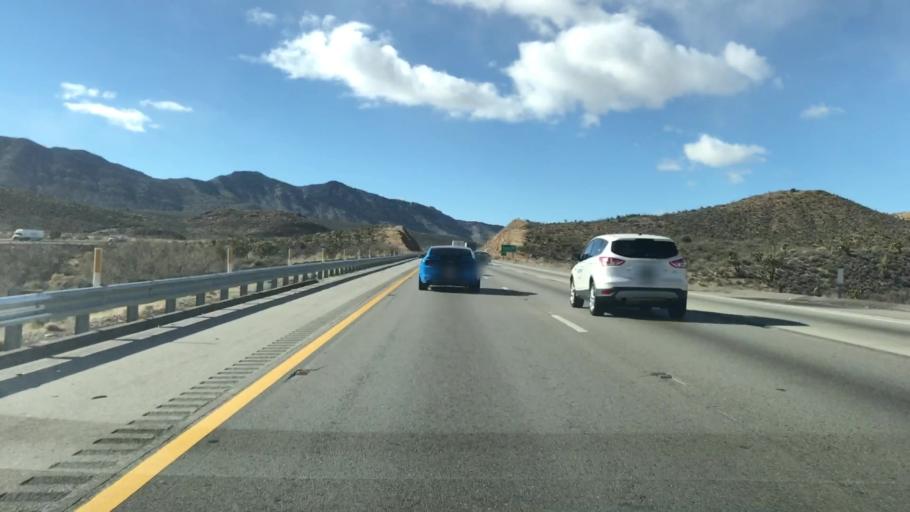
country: US
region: Nevada
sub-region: Clark County
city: Sandy Valley
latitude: 35.4708
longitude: -115.5079
